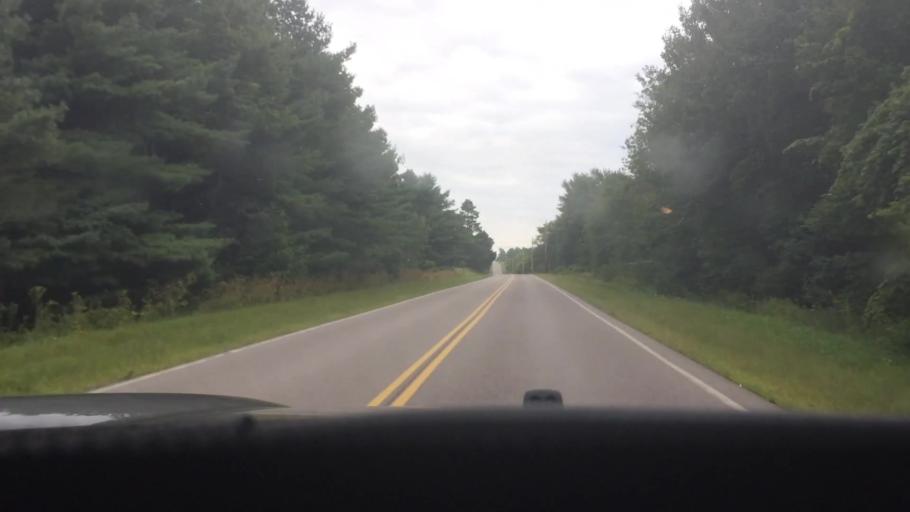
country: US
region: New York
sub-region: St. Lawrence County
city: Hannawa Falls
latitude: 44.5380
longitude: -75.0519
